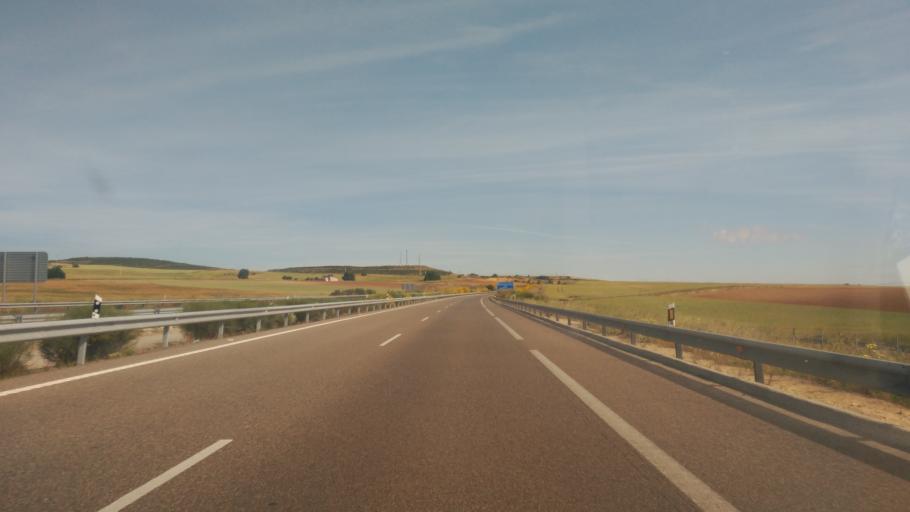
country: ES
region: Castille and Leon
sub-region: Provincia de Zamora
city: Corrales
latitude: 41.3676
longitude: -5.7166
